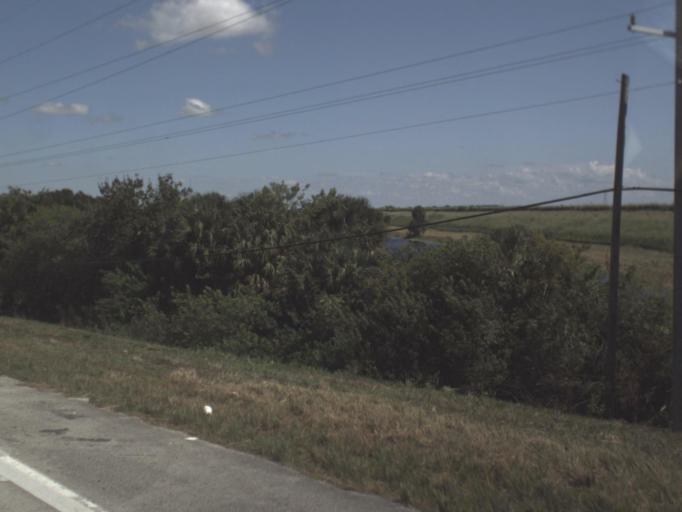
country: US
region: Florida
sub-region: Glades County
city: Moore Haven
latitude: 26.9718
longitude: -81.1175
